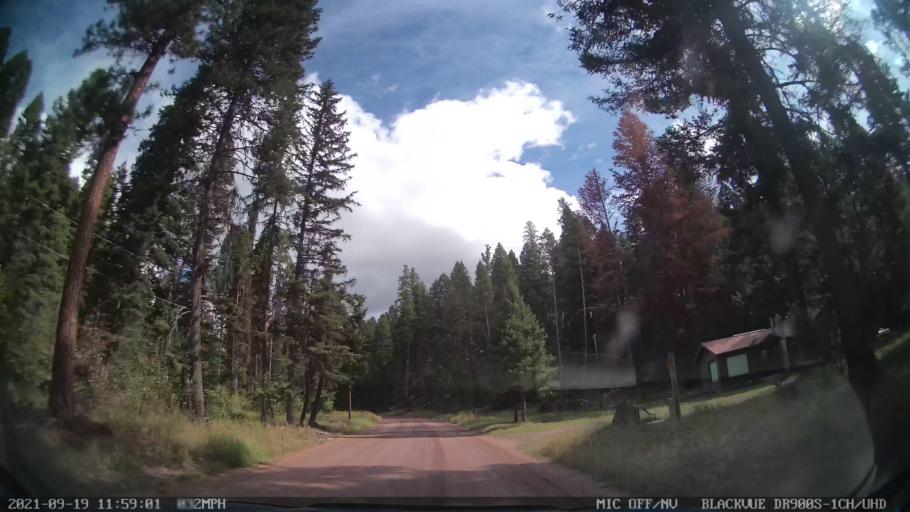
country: US
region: Montana
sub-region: Missoula County
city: Seeley Lake
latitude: 47.1831
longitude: -113.4804
